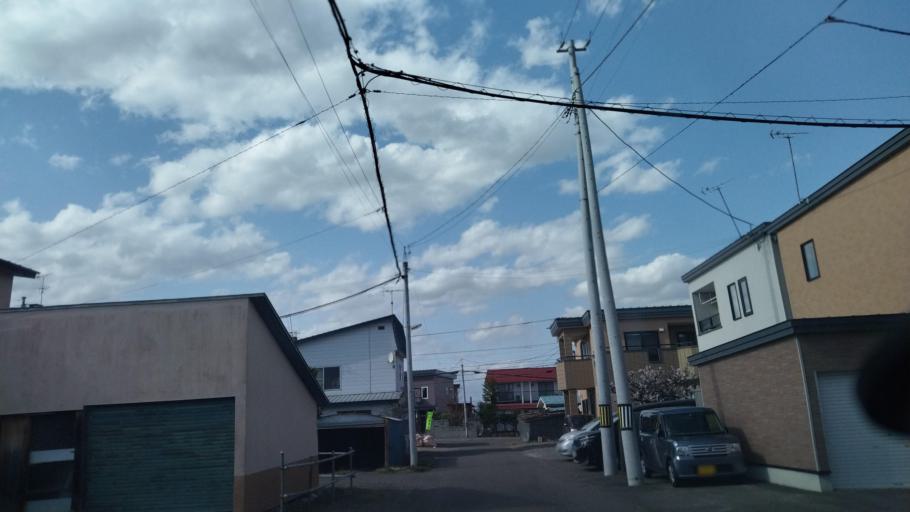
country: JP
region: Hokkaido
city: Obihiro
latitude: 42.9313
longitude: 143.1677
